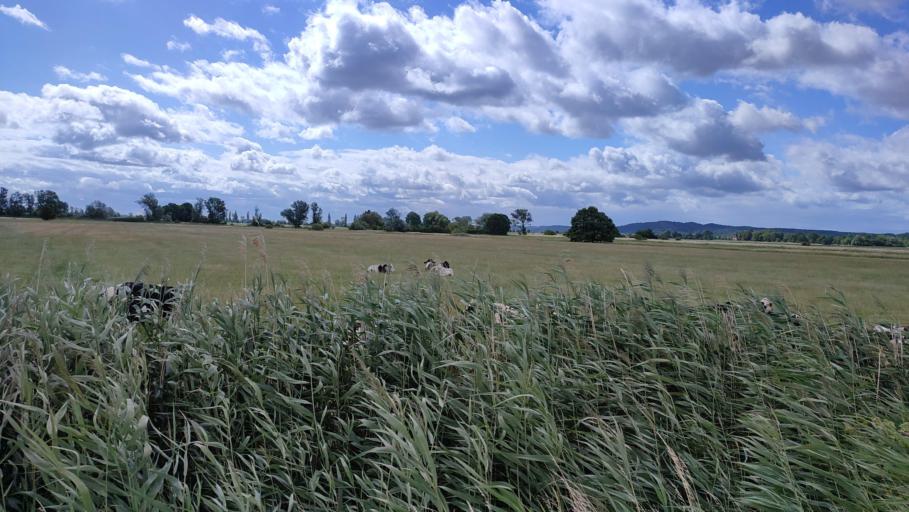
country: DE
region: Lower Saxony
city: Neu Darchau
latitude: 53.2251
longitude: 10.9515
